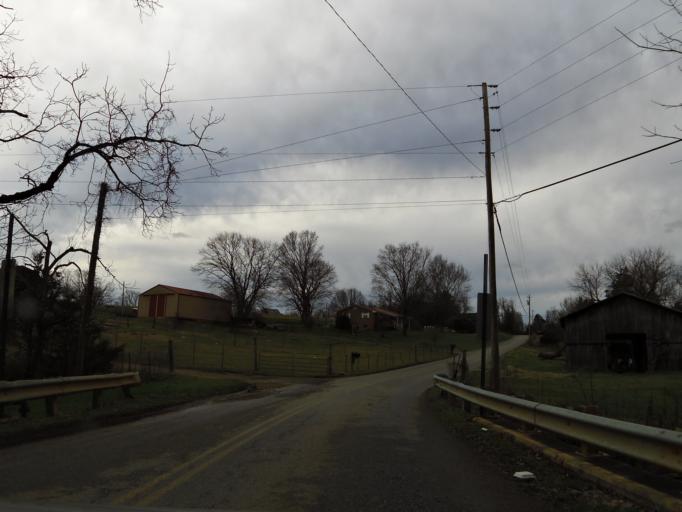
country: US
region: Tennessee
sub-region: Greene County
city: Tusculum
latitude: 36.2033
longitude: -82.7440
